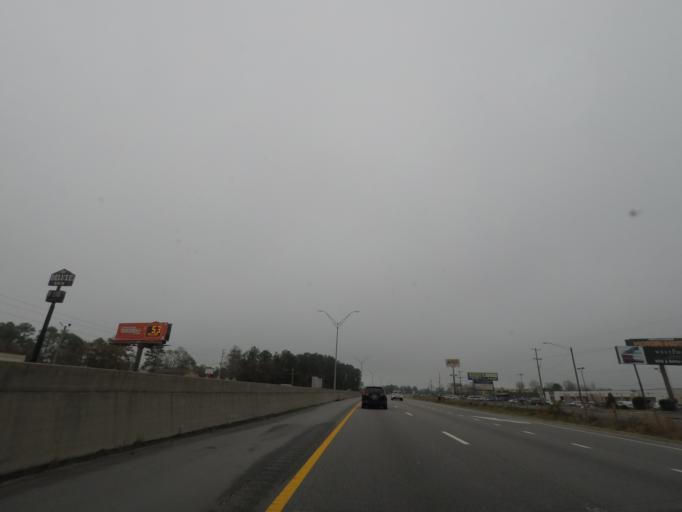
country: US
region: North Carolina
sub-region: Robeson County
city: Lumberton
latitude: 34.6437
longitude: -79.0149
